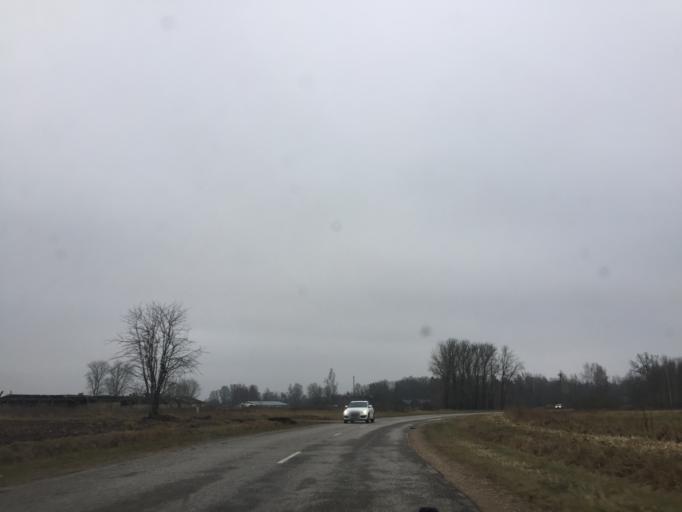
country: LV
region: Limbazu Rajons
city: Limbazi
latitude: 57.5250
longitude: 24.6902
